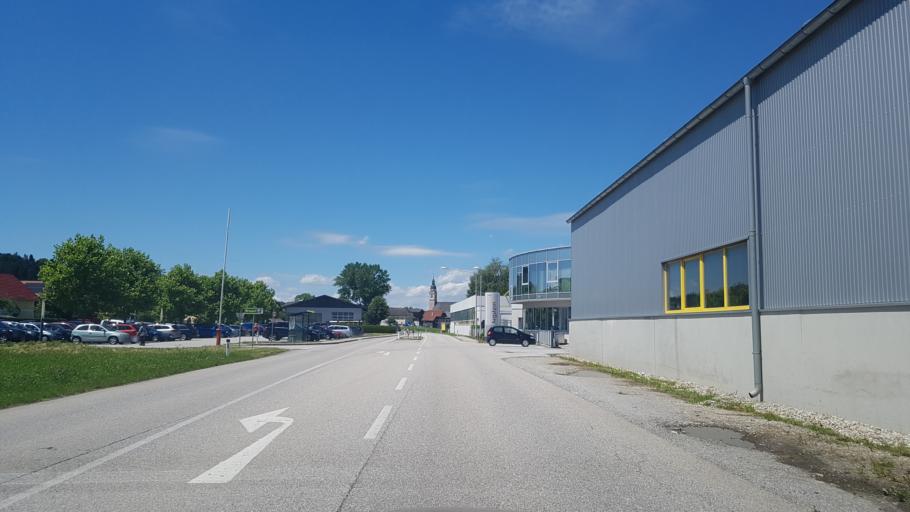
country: AT
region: Salzburg
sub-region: Politischer Bezirk Salzburg-Umgebung
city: Strasswalchen
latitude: 48.0017
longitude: 13.2234
